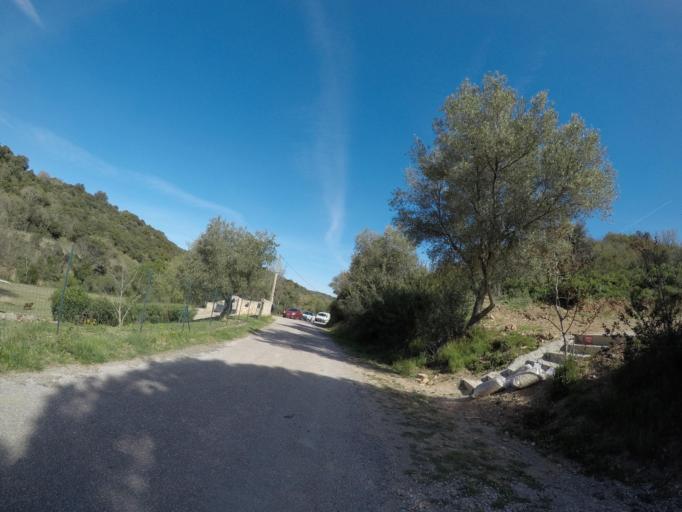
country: FR
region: Languedoc-Roussillon
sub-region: Departement des Pyrenees-Orientales
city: Thuir
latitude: 42.6347
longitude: 2.7004
